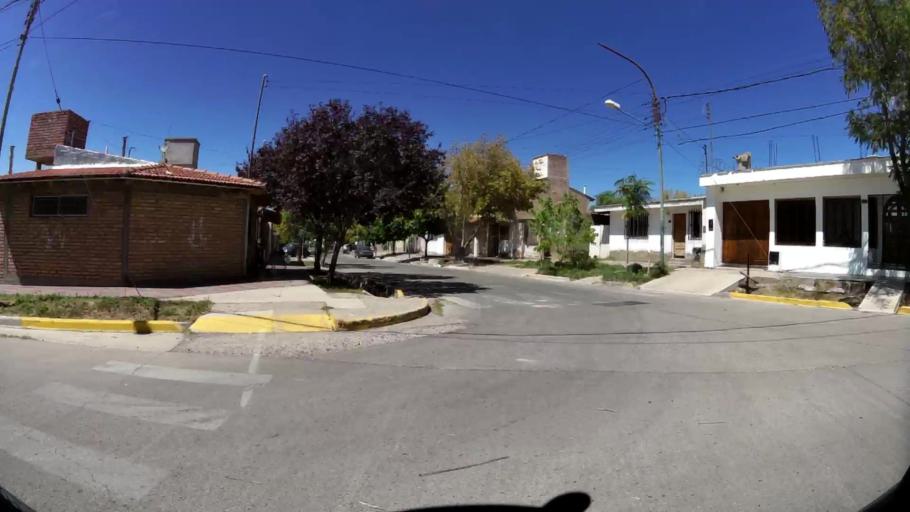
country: AR
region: Mendoza
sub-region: Departamento de Godoy Cruz
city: Godoy Cruz
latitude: -32.9489
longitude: -68.8641
